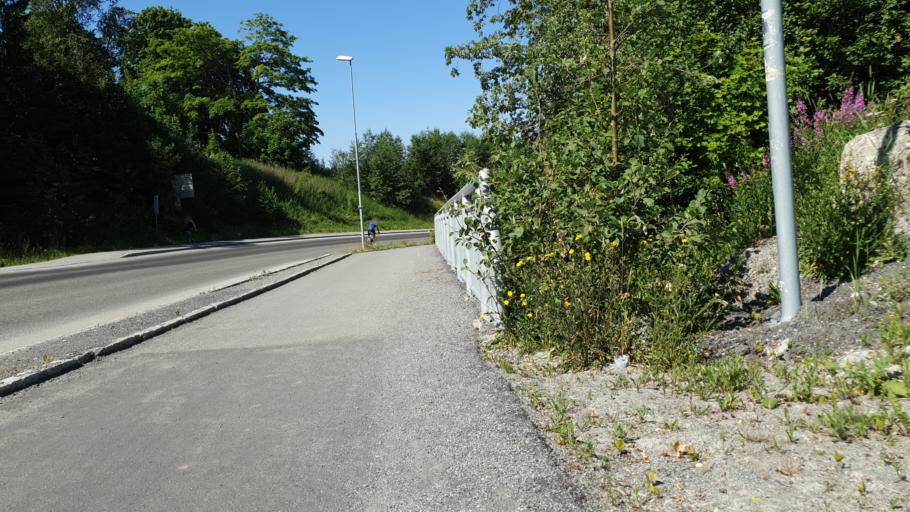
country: NO
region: Sor-Trondelag
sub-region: Trondheim
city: Trondheim
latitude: 63.4256
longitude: 10.5314
